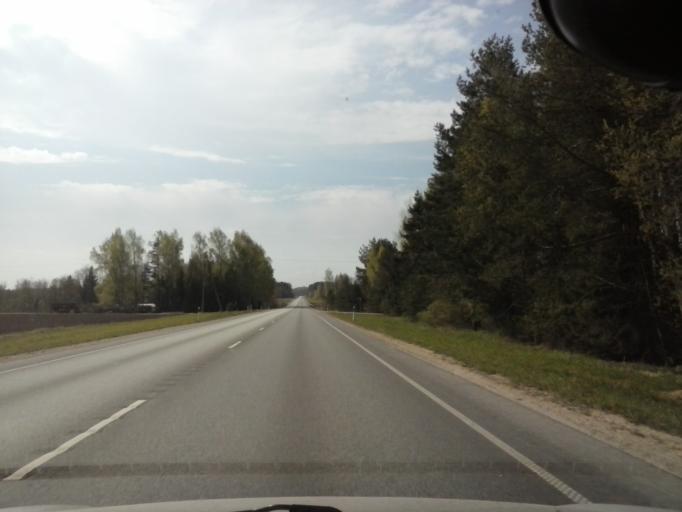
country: EE
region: Tartu
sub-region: UElenurme vald
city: Ulenurme
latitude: 58.2239
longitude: 26.7009
